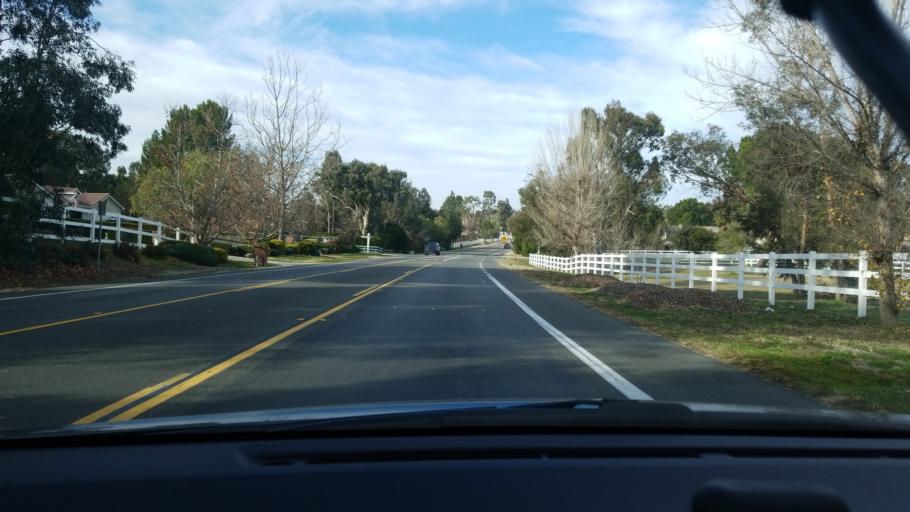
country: US
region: California
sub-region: Riverside County
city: Temecula
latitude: 33.4842
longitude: -117.1353
